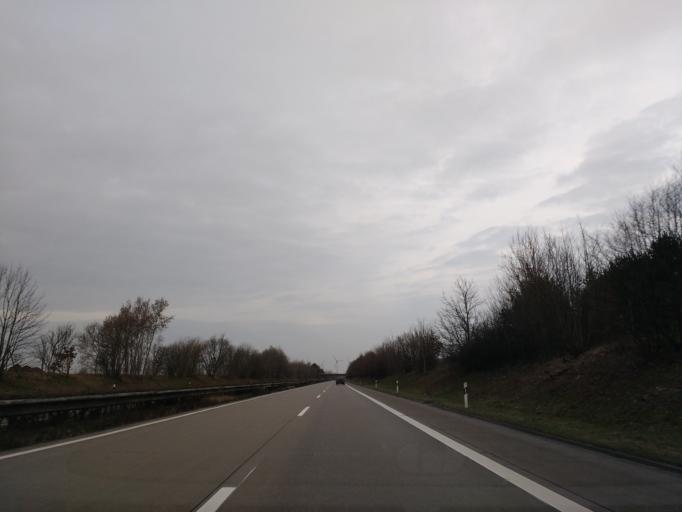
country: DE
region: Lower Saxony
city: Langen
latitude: 53.6534
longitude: 8.6609
